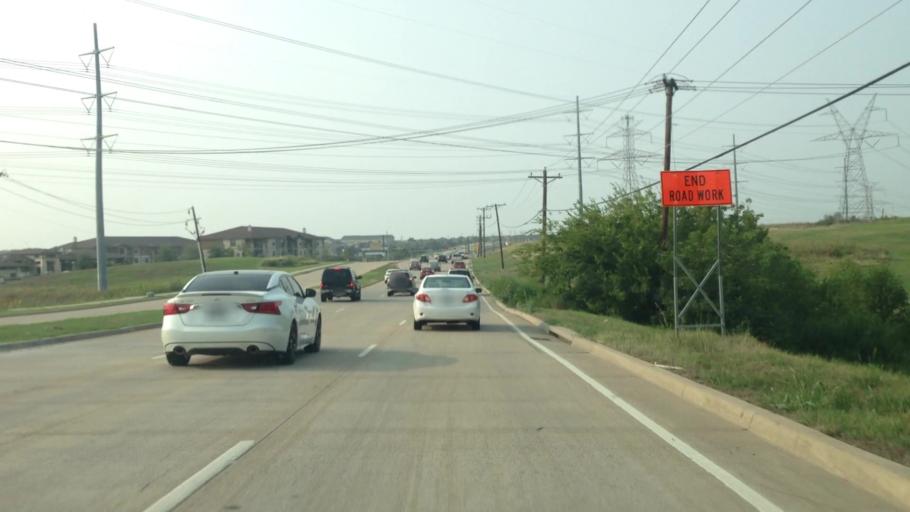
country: US
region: Texas
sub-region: Denton County
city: The Colony
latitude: 33.0234
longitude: -96.9163
